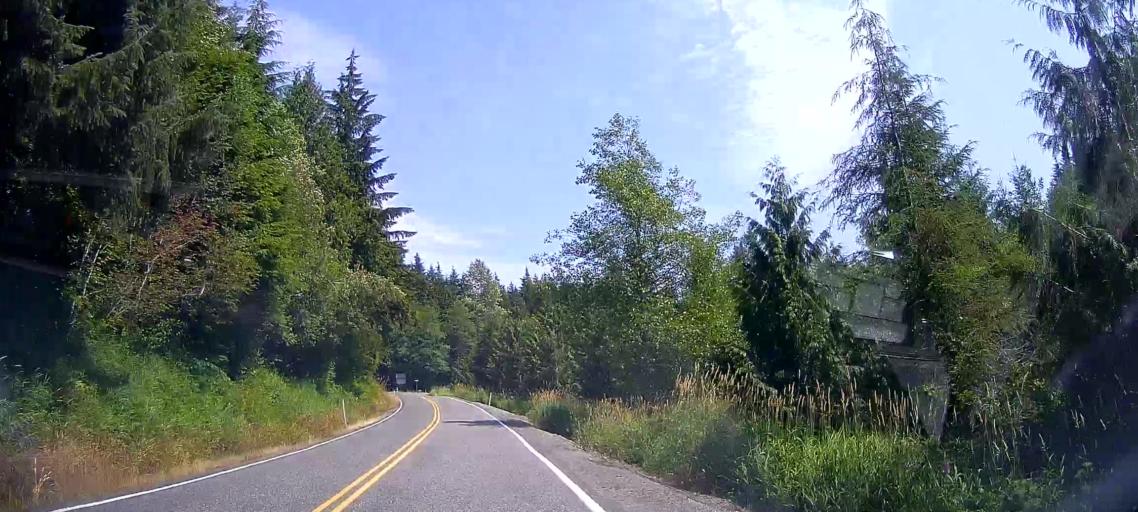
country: US
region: Washington
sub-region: Snohomish County
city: Arlington Heights
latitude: 48.3359
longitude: -122.0374
